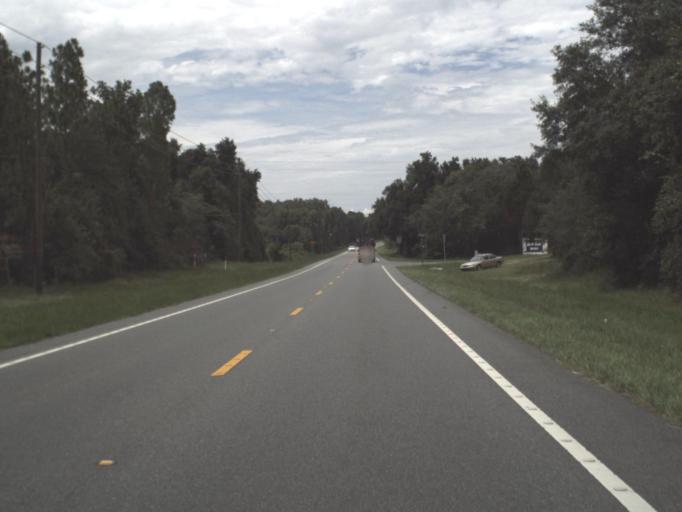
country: US
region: Florida
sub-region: Citrus County
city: Hernando
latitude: 28.9543
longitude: -82.3775
